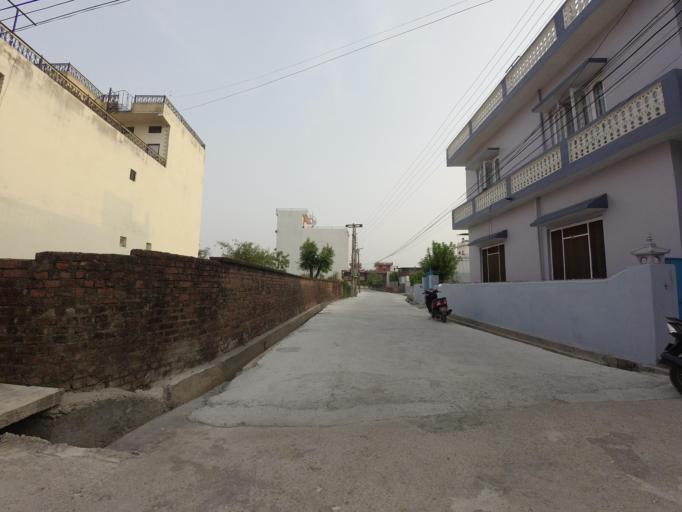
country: NP
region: Western Region
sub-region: Lumbini Zone
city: Bhairahawa
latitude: 27.5130
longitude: 83.4570
